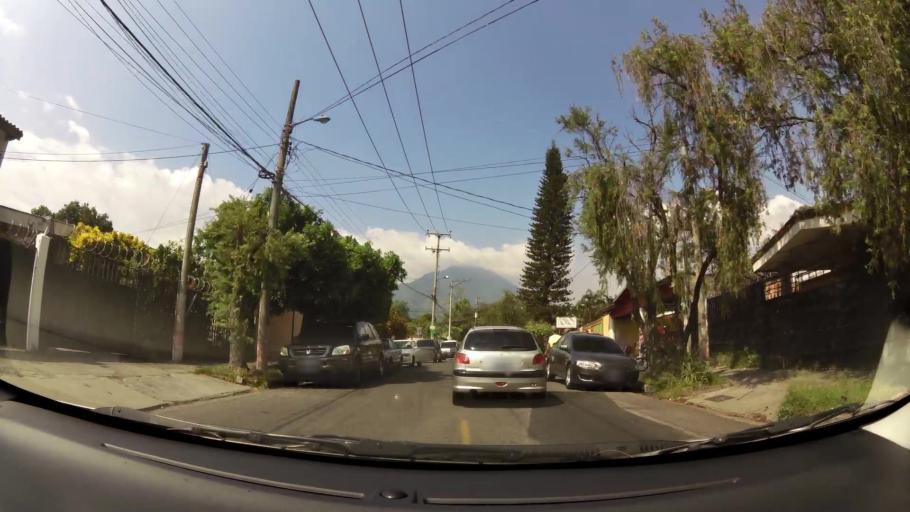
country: SV
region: San Salvador
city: Mejicanos
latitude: 13.7087
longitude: -89.2183
